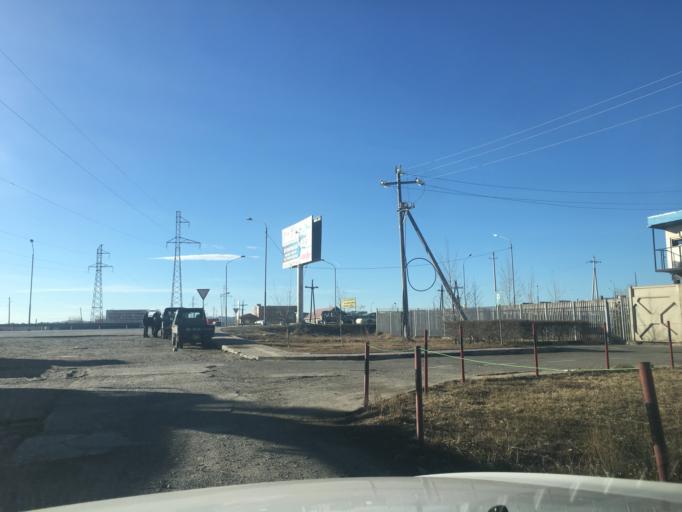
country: MN
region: Ulaanbaatar
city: Ulaanbaatar
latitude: 47.9011
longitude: 106.7867
